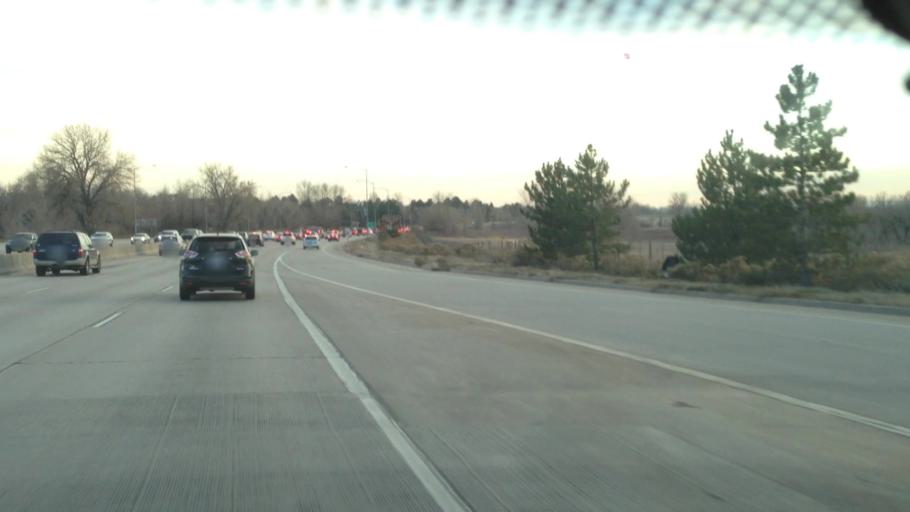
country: US
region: Colorado
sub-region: Arapahoe County
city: Dove Valley
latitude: 39.6514
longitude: -104.8305
